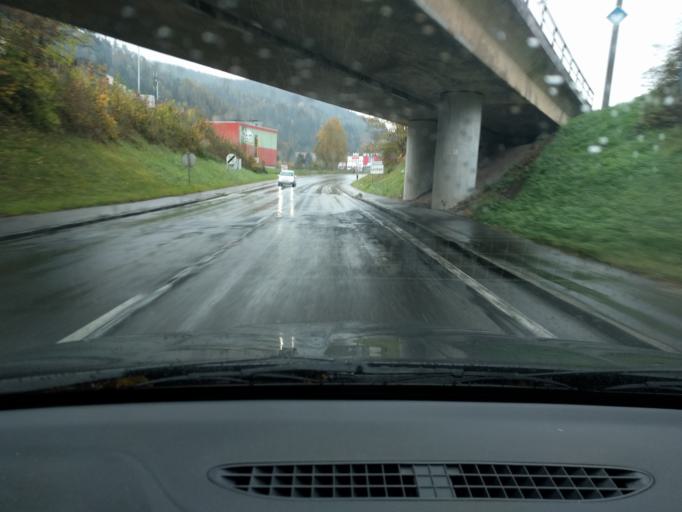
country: AT
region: Styria
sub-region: Politischer Bezirk Leoben
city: Proleb
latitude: 47.3861
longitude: 15.1289
